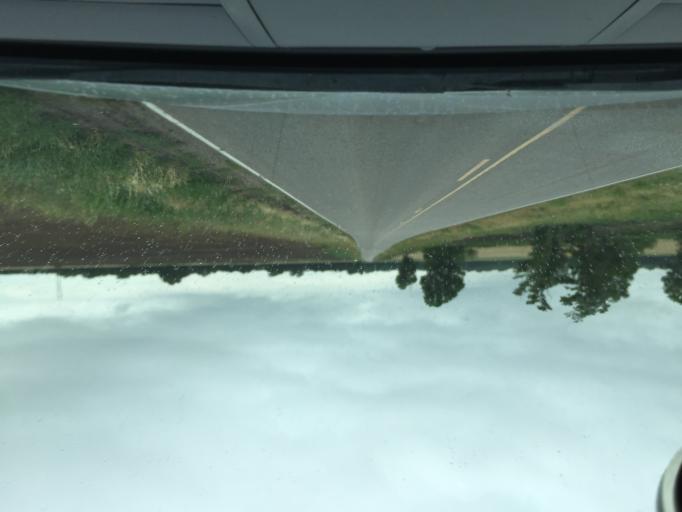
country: US
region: Kansas
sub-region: Reno County
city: Buhler
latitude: 38.1446
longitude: -97.8153
